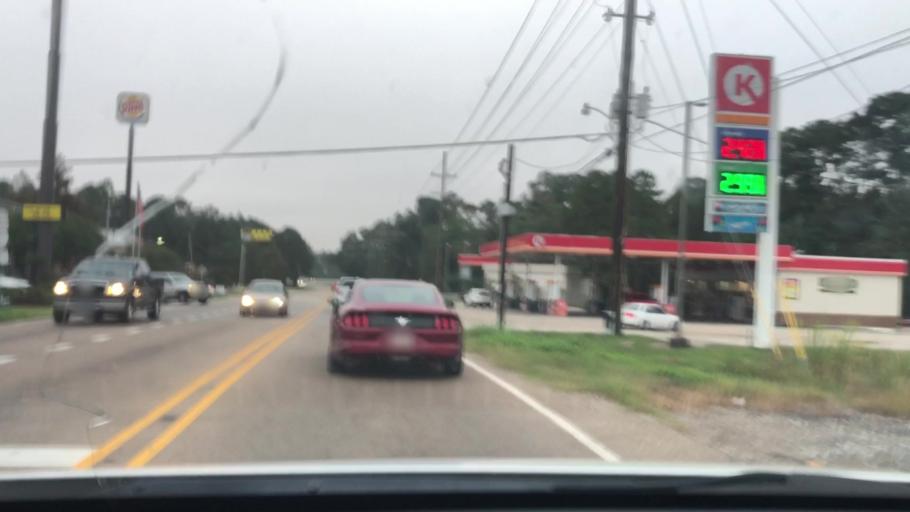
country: US
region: Louisiana
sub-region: Saint Tammany Parish
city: Slidell
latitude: 30.3115
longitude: -89.7696
